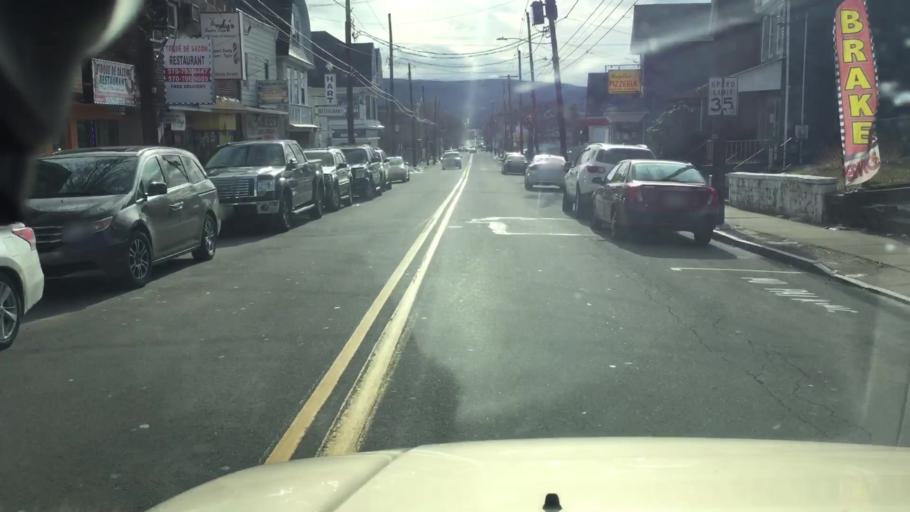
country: US
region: Pennsylvania
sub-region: Luzerne County
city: Ashley
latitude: 41.2293
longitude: -75.8919
